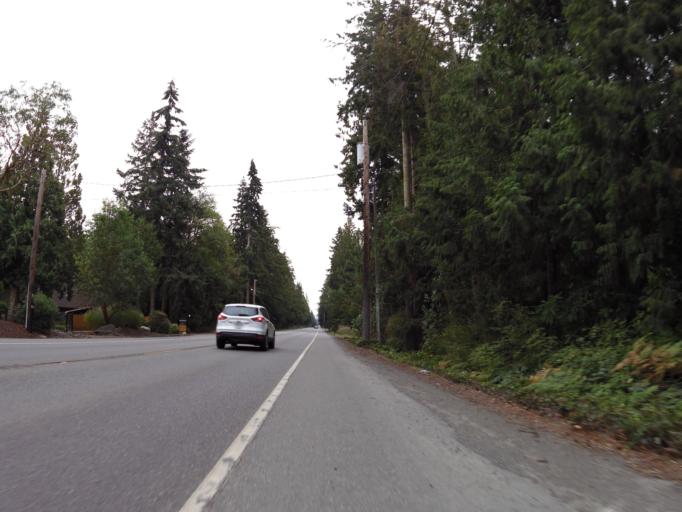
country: US
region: Washington
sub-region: Jefferson County
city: Port Hadlock-Irondale
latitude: 48.0642
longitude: -122.8119
